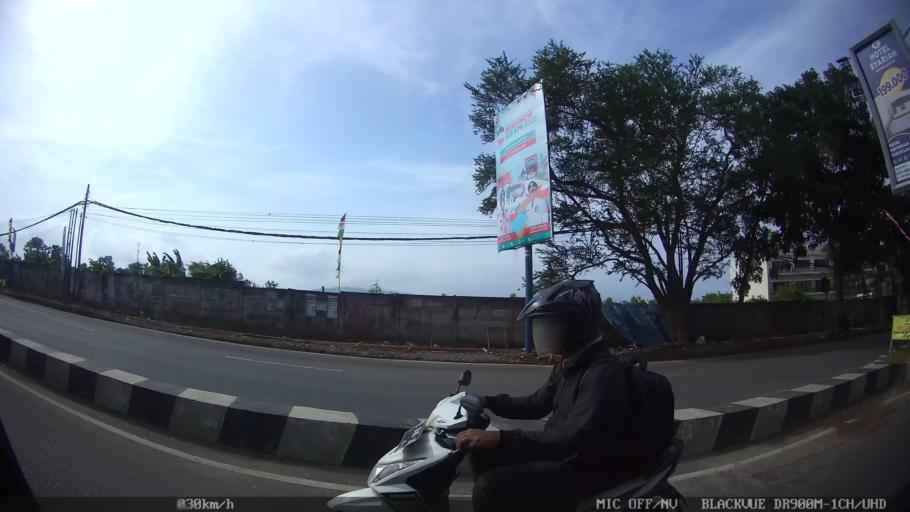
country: ID
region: Lampung
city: Kedaton
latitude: -5.3821
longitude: 105.2840
